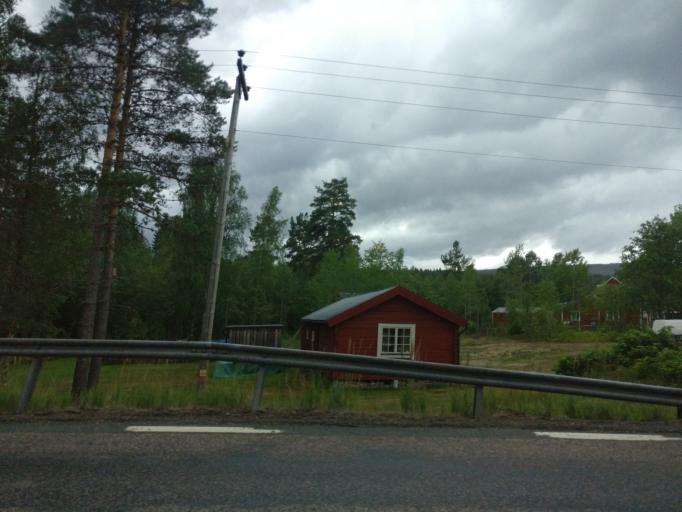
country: SE
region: Vaermland
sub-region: Torsby Kommun
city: Torsby
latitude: 60.6302
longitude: 13.0207
